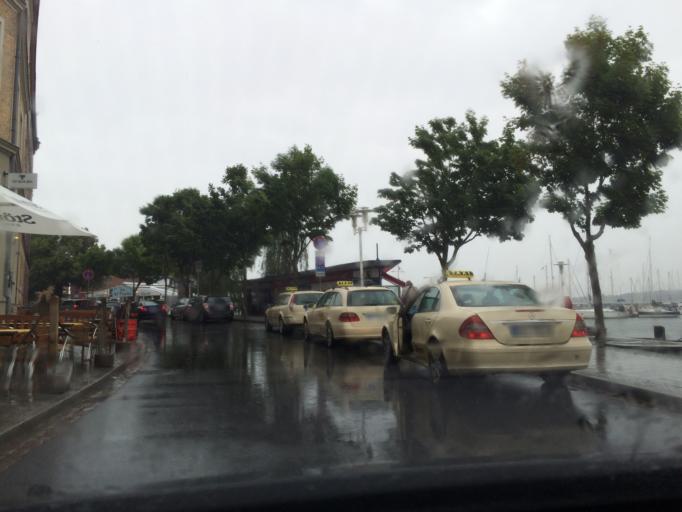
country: DE
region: Mecklenburg-Vorpommern
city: Stralsund
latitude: 54.3169
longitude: 13.0947
